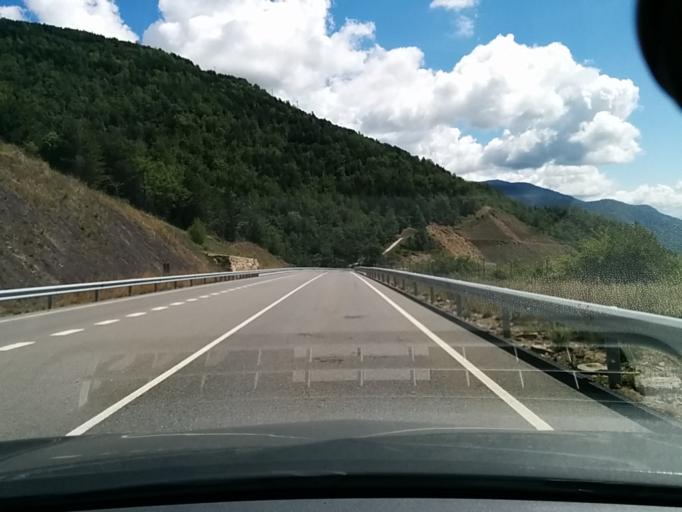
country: ES
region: Aragon
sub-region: Provincia de Huesca
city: Fiscal
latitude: 42.5004
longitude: -0.1503
